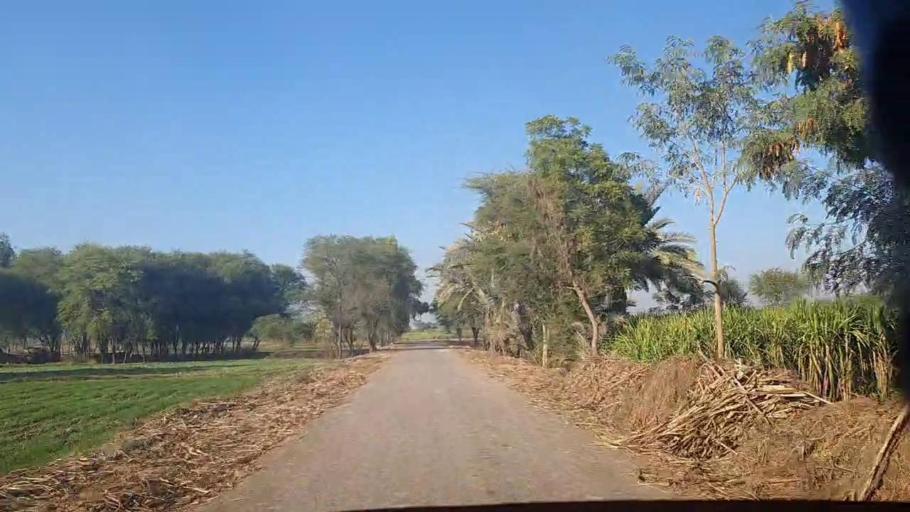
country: PK
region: Sindh
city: Sobhadero
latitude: 27.3890
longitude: 68.4191
